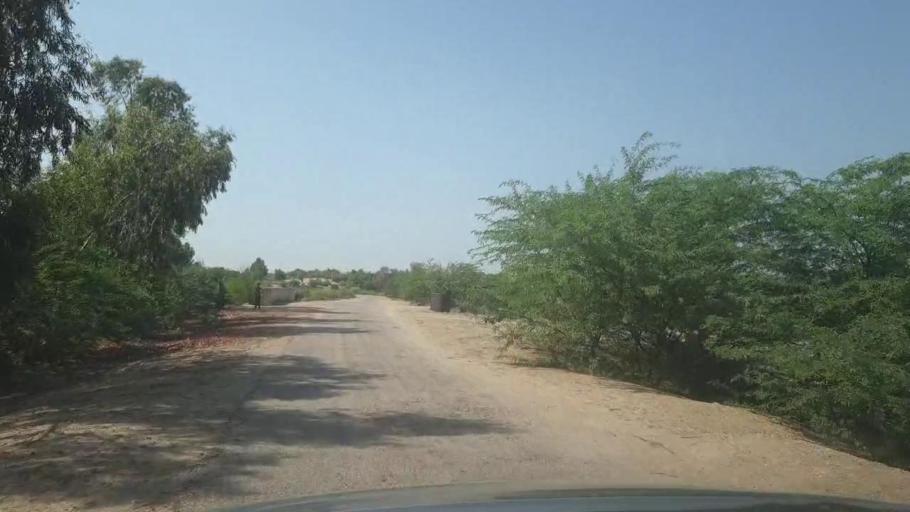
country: PK
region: Sindh
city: Rohri
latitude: 27.4327
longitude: 69.0765
